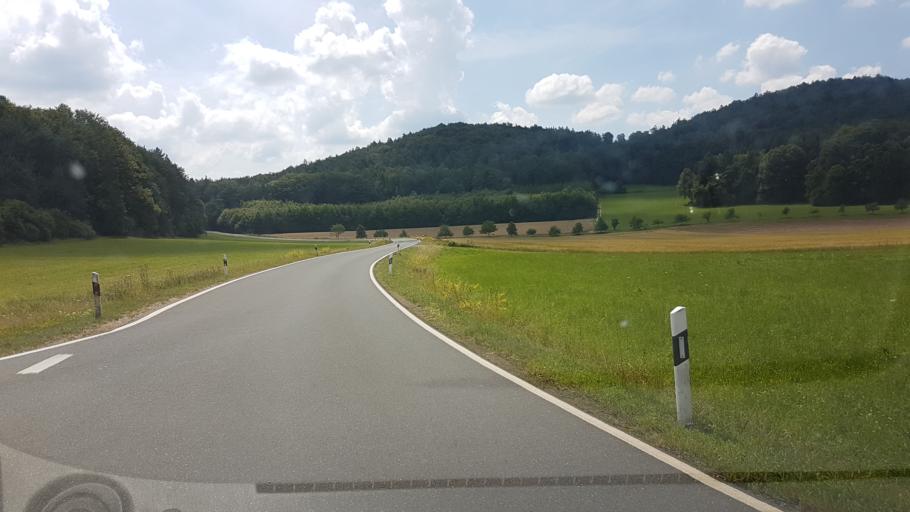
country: DE
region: Bavaria
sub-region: Upper Franconia
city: Gossweinstein
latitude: 49.7728
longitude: 11.2836
